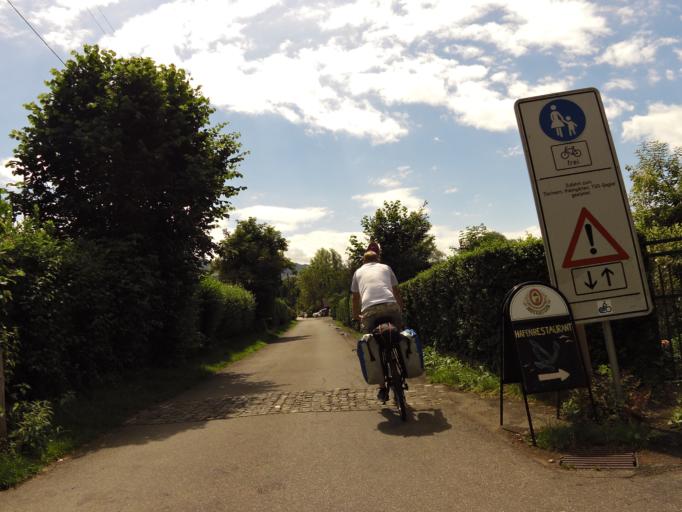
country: AT
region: Vorarlberg
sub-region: Politischer Bezirk Bregenz
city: Lochau
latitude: 47.5372
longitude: 9.7318
